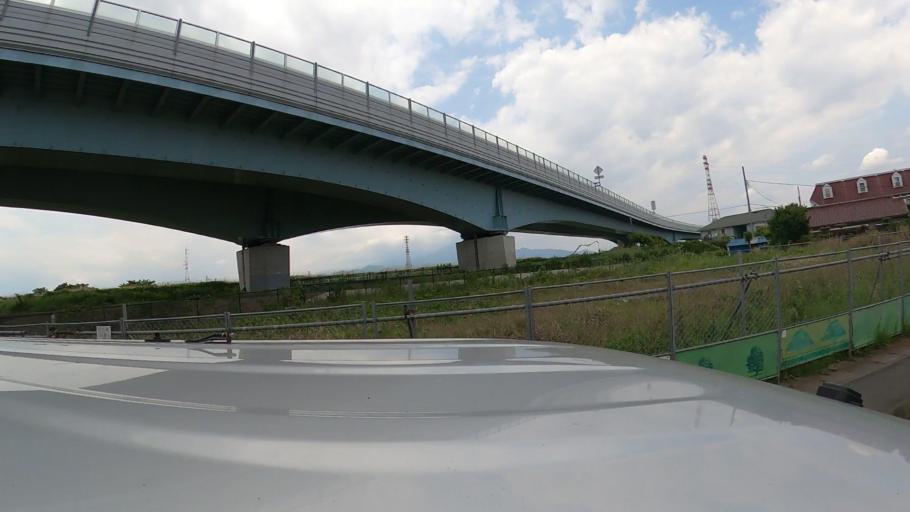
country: JP
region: Kanagawa
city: Chigasaki
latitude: 35.3636
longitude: 139.3740
